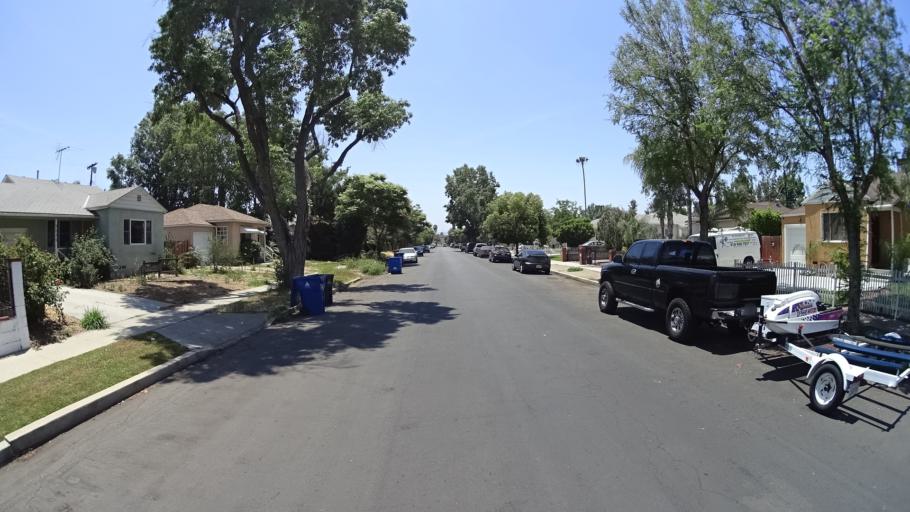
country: US
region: California
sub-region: Los Angeles County
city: Van Nuys
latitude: 34.2172
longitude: -118.4618
